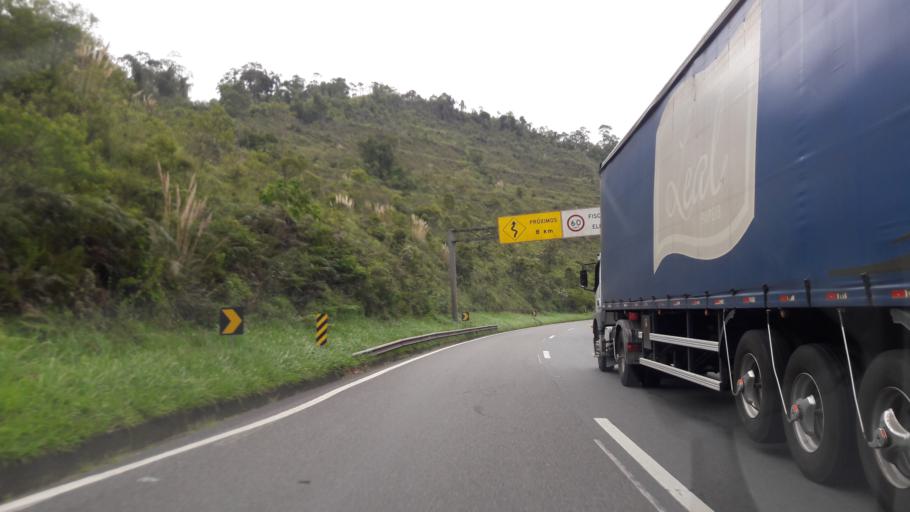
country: BR
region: Sao Paulo
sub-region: Cajati
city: Cajati
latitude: -24.9604
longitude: -48.4187
